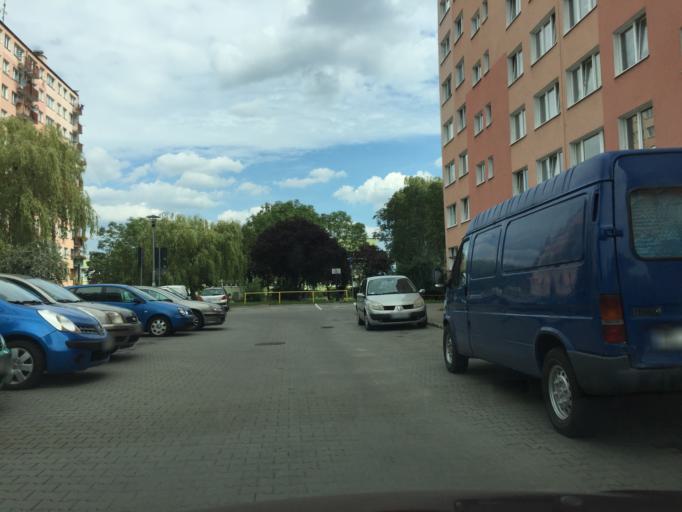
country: PL
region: Greater Poland Voivodeship
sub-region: Kalisz
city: Kalisz
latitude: 51.7463
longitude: 18.0698
